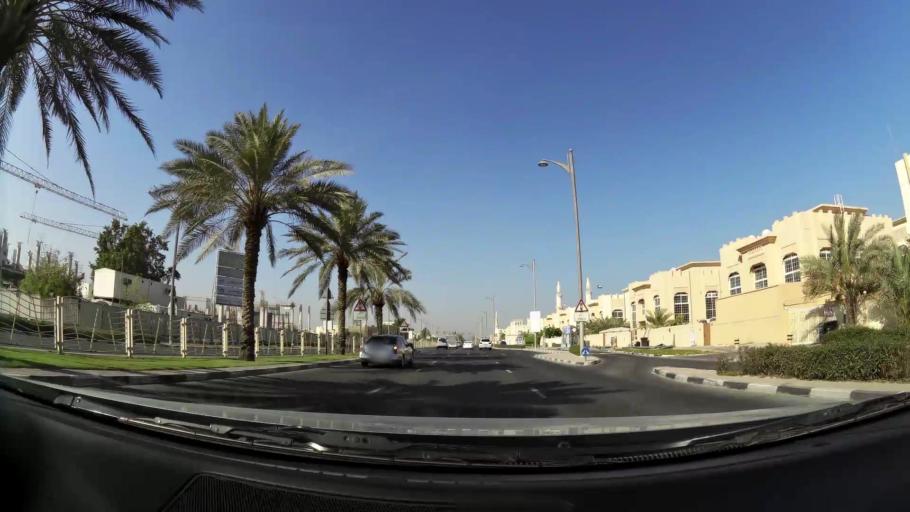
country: AE
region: Dubai
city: Dubai
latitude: 25.2117
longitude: 55.2478
